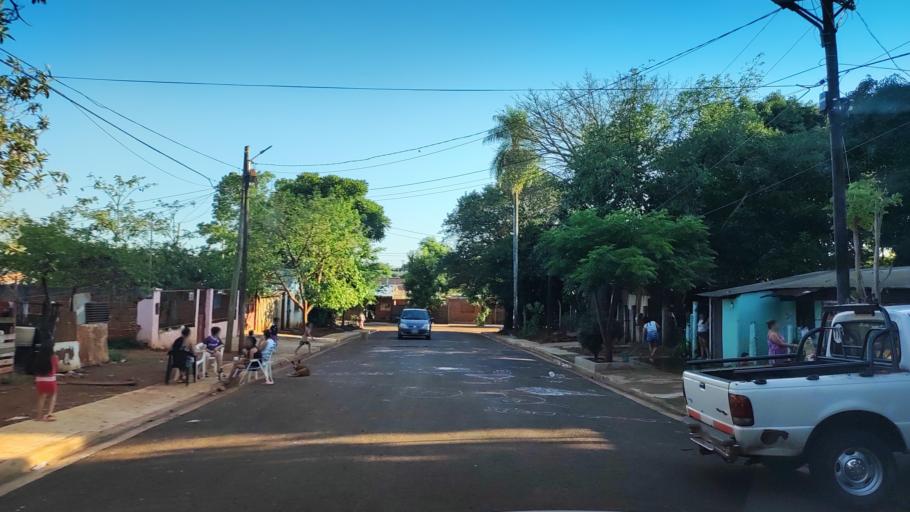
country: AR
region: Misiones
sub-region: Departamento de Capital
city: Posadas
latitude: -27.3823
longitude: -55.9281
